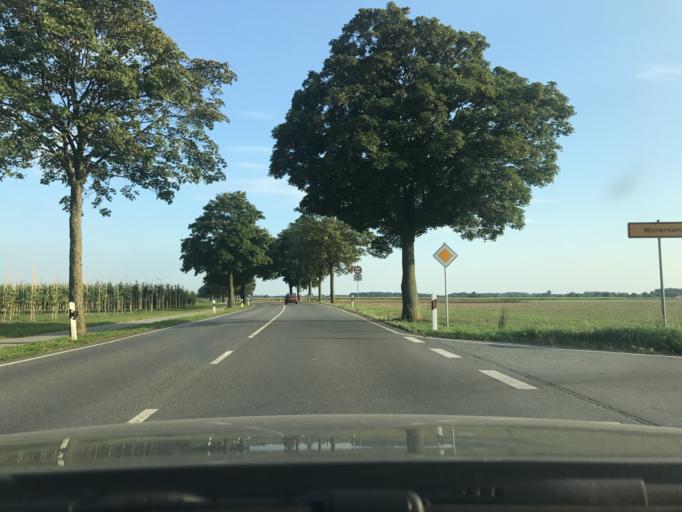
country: DE
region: North Rhine-Westphalia
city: Geldern
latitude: 51.4839
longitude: 6.3392
